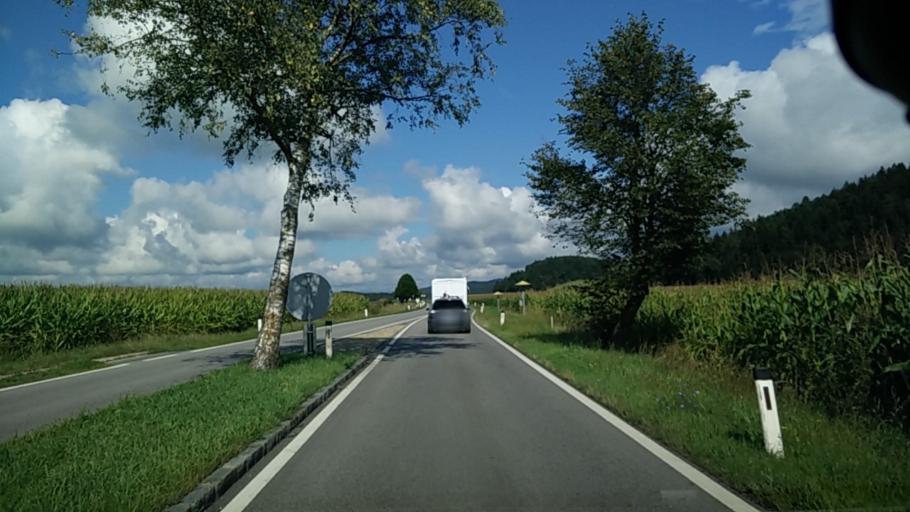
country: AT
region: Carinthia
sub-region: Politischer Bezirk Klagenfurt Land
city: Grafenstein
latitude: 46.6358
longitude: 14.5313
